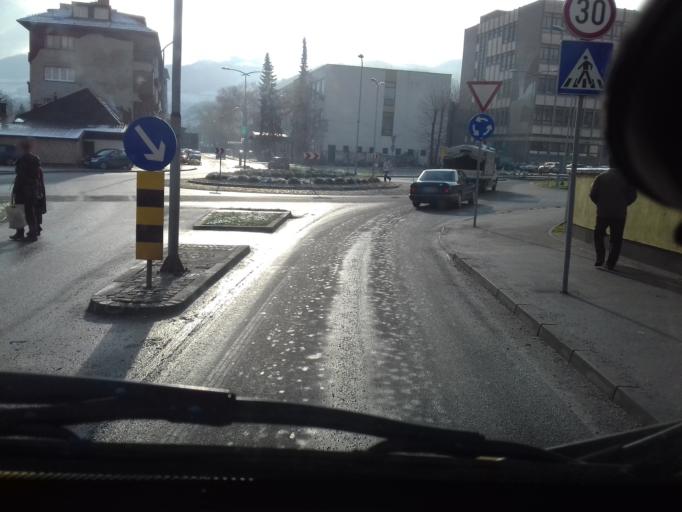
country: BA
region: Federation of Bosnia and Herzegovina
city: Zenica
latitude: 44.2017
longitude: 17.9022
